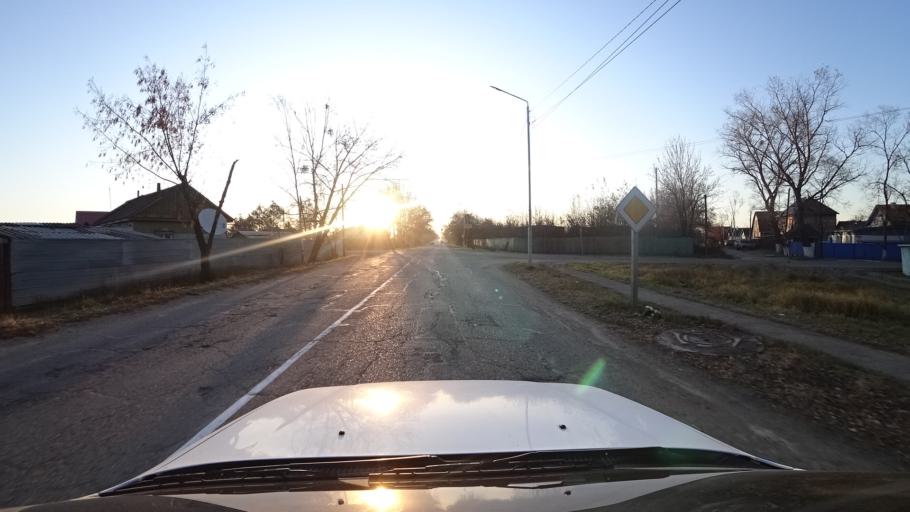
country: RU
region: Primorskiy
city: Dal'nerechensk
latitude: 45.9268
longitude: 133.7356
